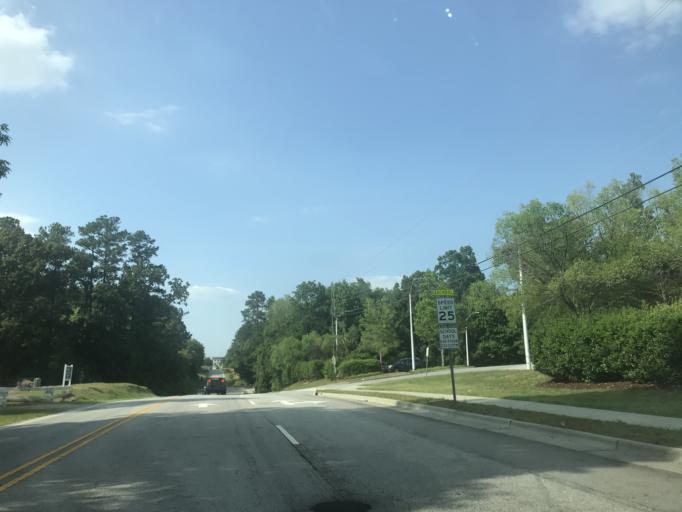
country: US
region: North Carolina
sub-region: Wake County
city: Knightdale
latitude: 35.8036
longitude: -78.4861
